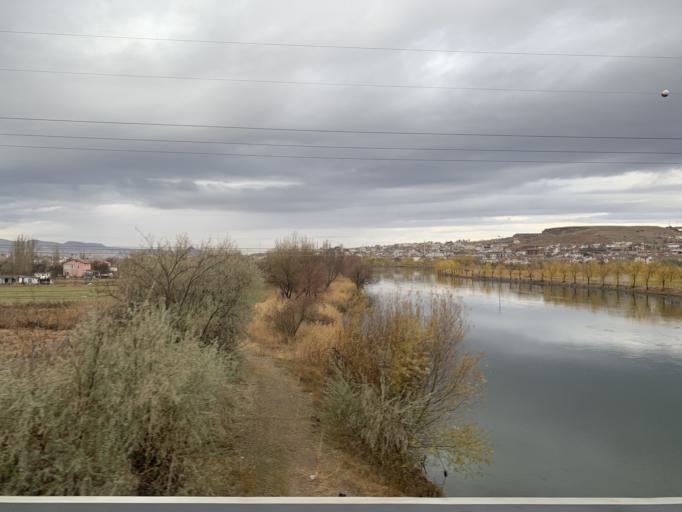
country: TR
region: Nevsehir
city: Avanos
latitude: 38.7159
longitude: 34.8595
